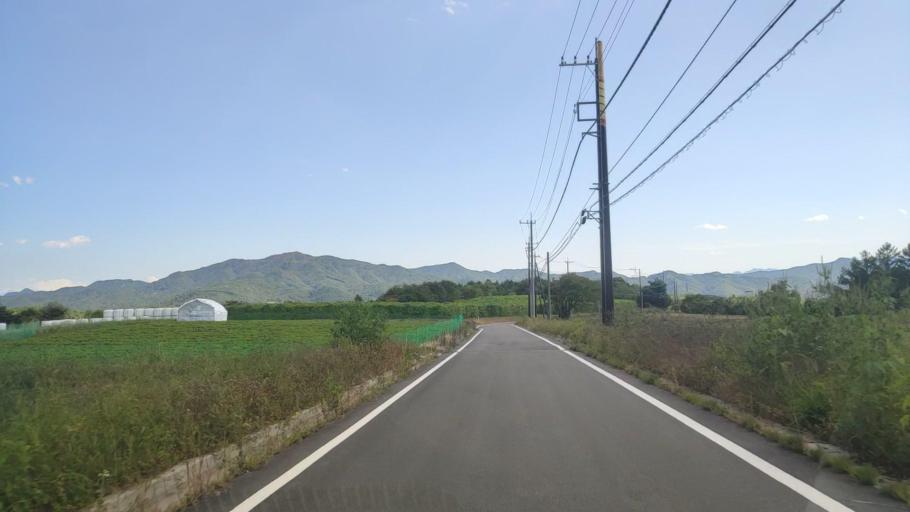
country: JP
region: Gunma
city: Nakanojomachi
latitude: 36.6439
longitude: 138.6169
